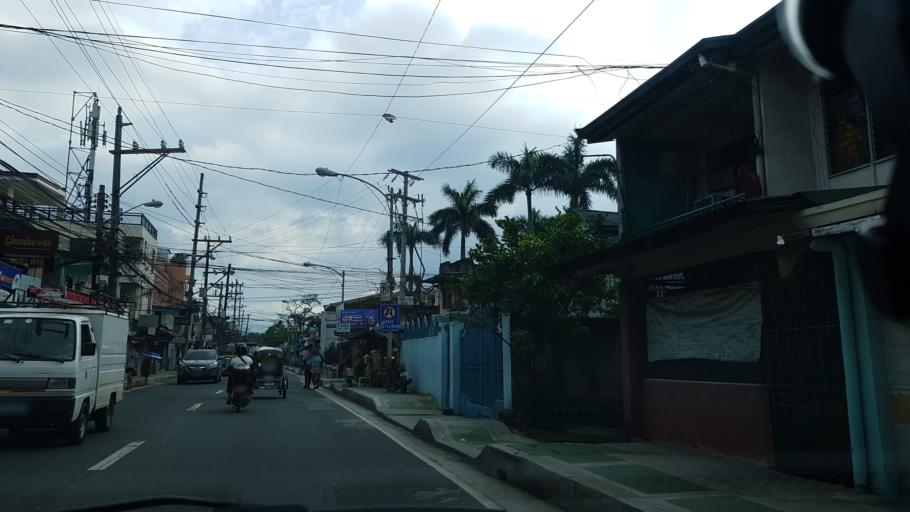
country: PH
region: Metro Manila
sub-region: Pasig
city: Pasig City
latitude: 14.5735
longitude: 121.0785
